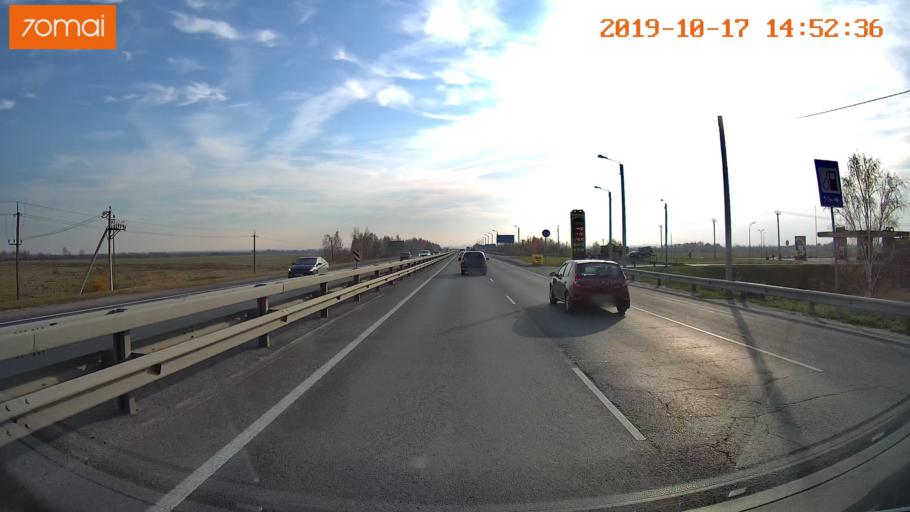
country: RU
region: Rjazan
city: Polyany
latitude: 54.7055
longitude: 39.8447
